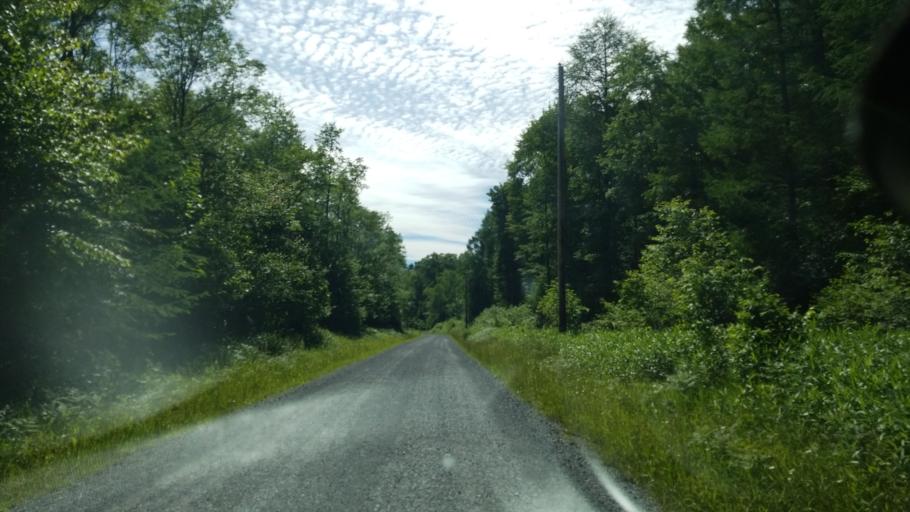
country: US
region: Pennsylvania
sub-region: Clearfield County
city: Clearfield
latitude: 41.1920
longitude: -78.4734
